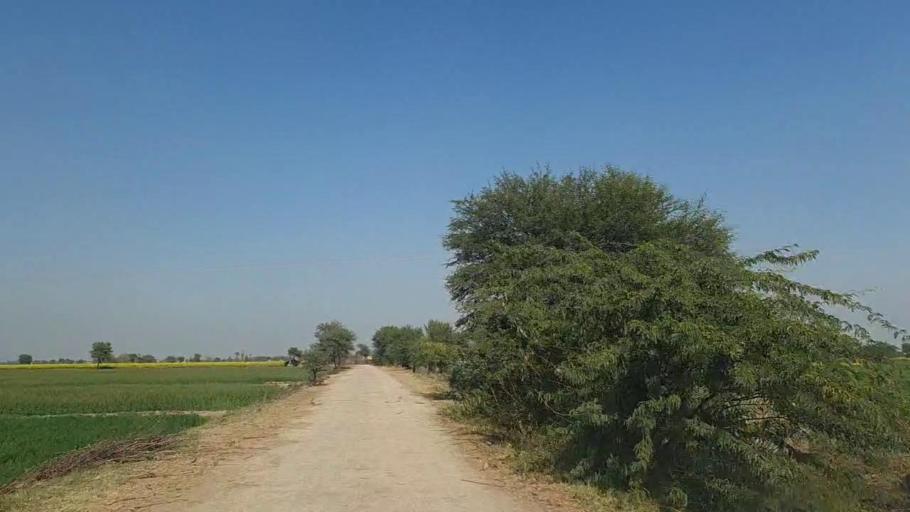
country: PK
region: Sindh
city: Shahpur Chakar
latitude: 26.1890
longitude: 68.6048
